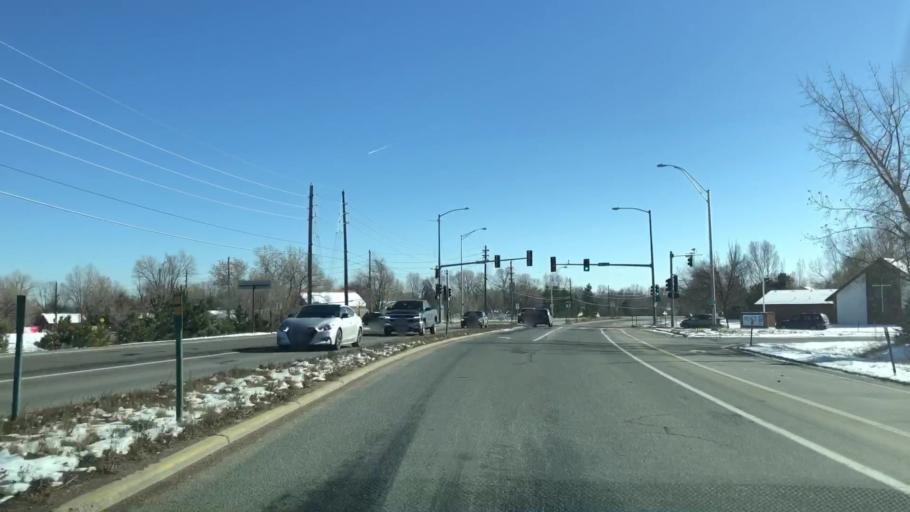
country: US
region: Colorado
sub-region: Boulder County
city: Boulder
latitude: 40.0516
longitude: -105.2607
